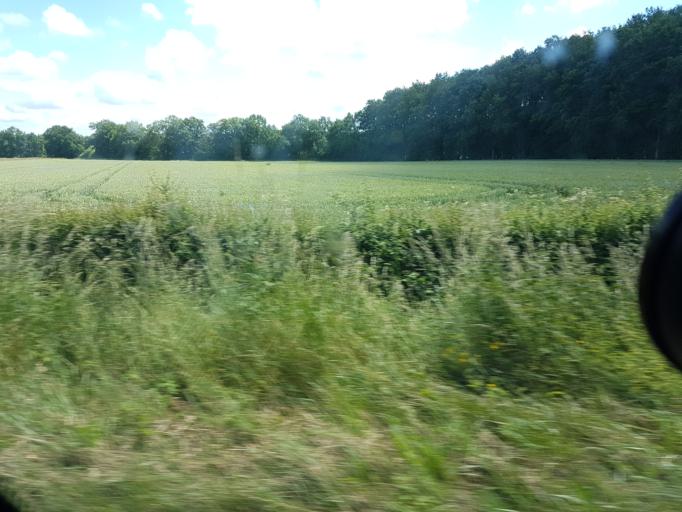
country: FR
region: Bourgogne
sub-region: Departement de Saone-et-Loire
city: Epinac
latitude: 46.9907
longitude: 4.4833
